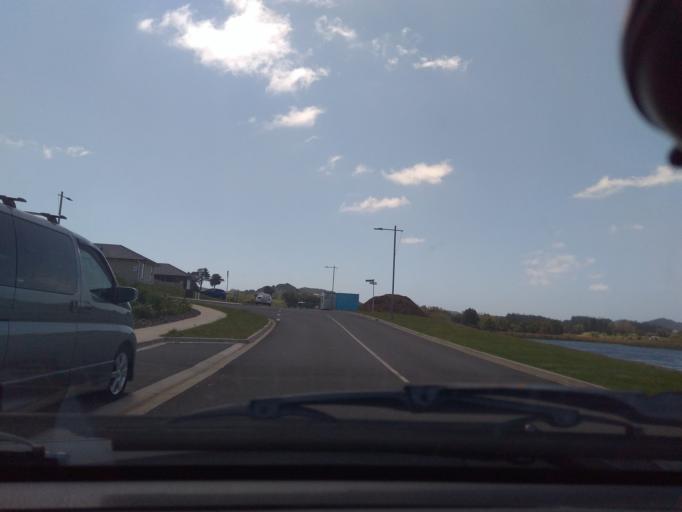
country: NZ
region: Northland
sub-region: Whangarei
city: Whangarei
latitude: -35.6762
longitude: 174.3196
